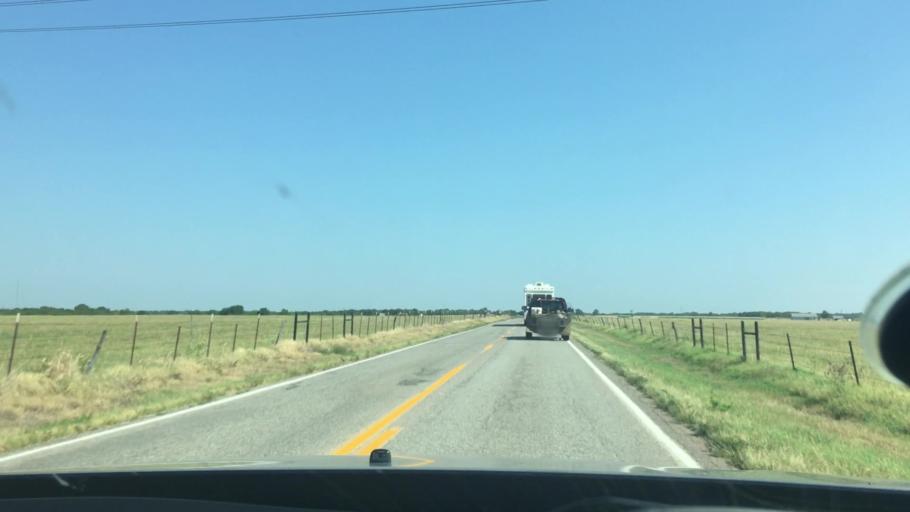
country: US
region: Oklahoma
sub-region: Johnston County
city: Tishomingo
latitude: 34.1662
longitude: -96.5089
